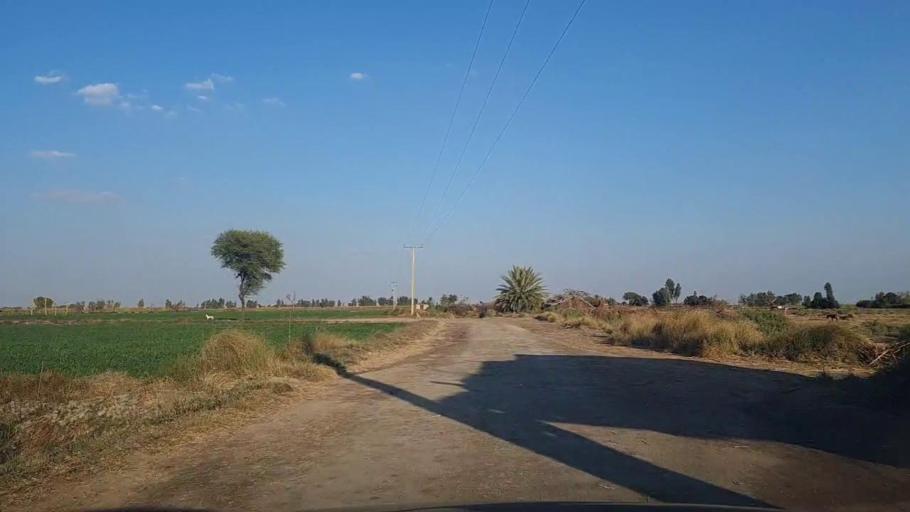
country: PK
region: Sindh
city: Sanghar
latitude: 25.9194
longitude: 69.0480
